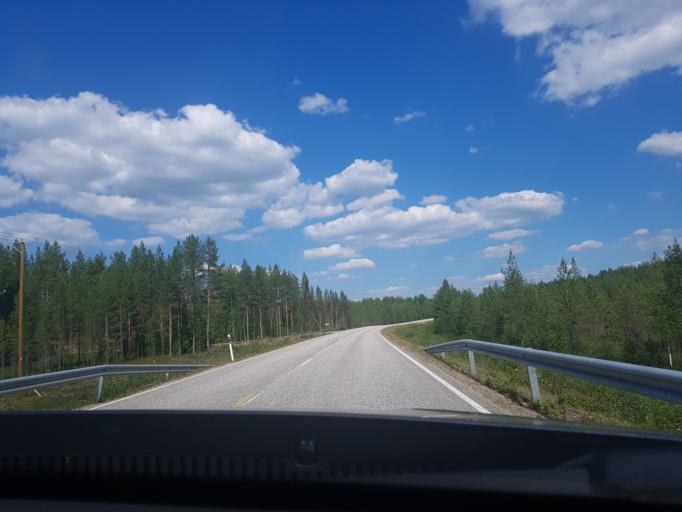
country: FI
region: Kainuu
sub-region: Kehys-Kainuu
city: Kuhmo
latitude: 64.2229
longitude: 29.8013
